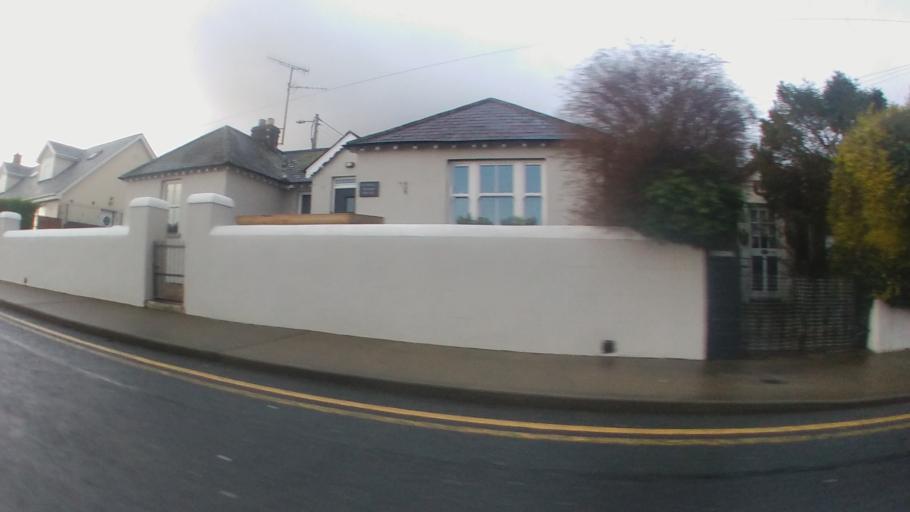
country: IE
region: Leinster
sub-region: Wicklow
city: Kilcoole
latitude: 53.1095
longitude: -6.0650
